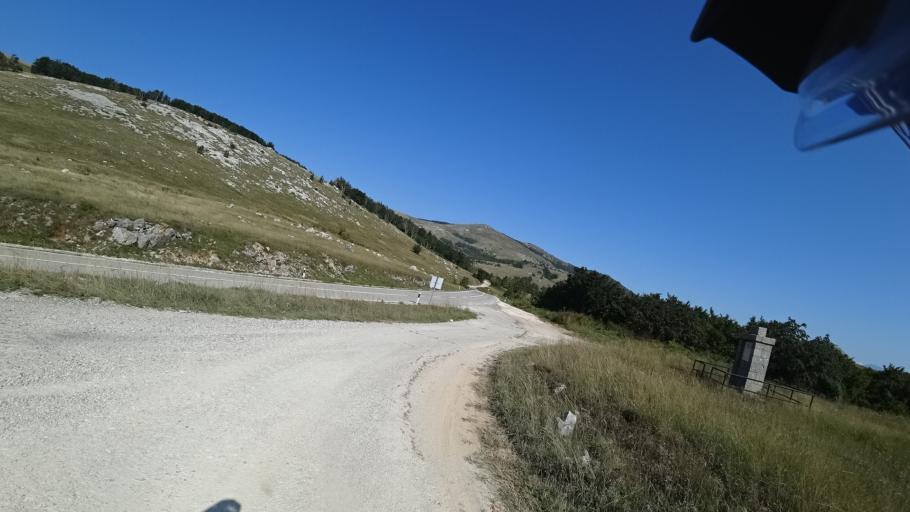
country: HR
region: Zadarska
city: Gracac
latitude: 44.2977
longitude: 16.0889
